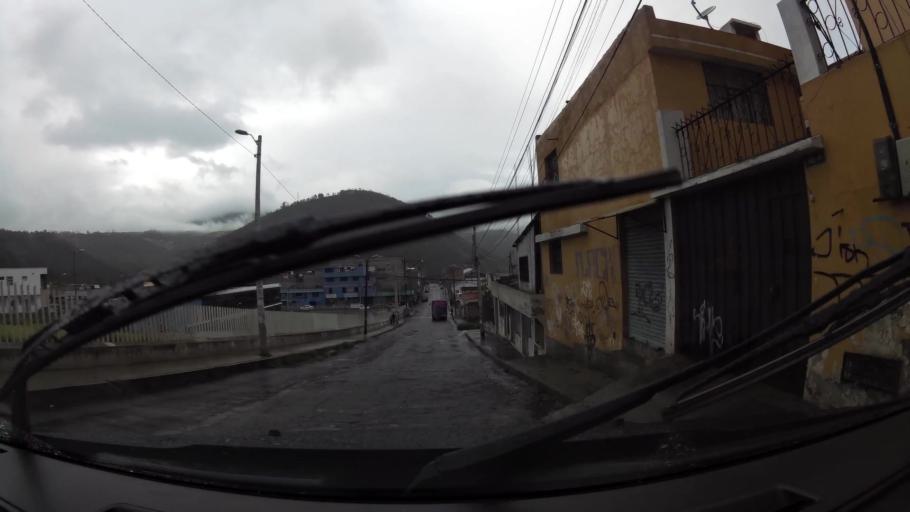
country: EC
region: Pichincha
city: Quito
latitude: -0.0864
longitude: -78.5102
